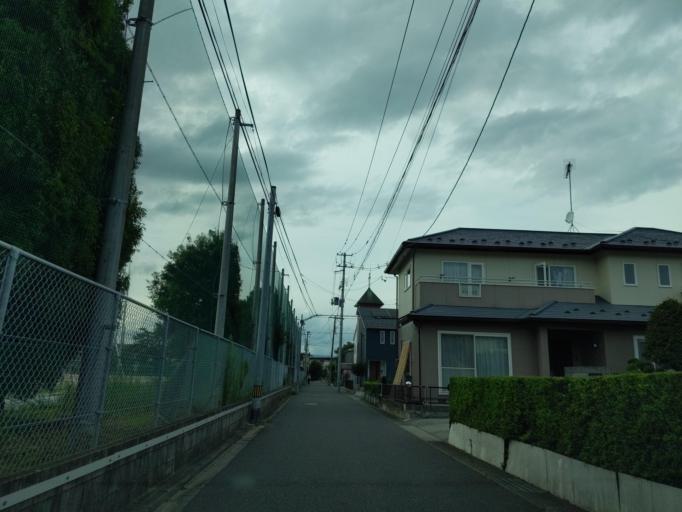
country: JP
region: Fukushima
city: Koriyama
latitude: 37.4026
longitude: 140.3390
